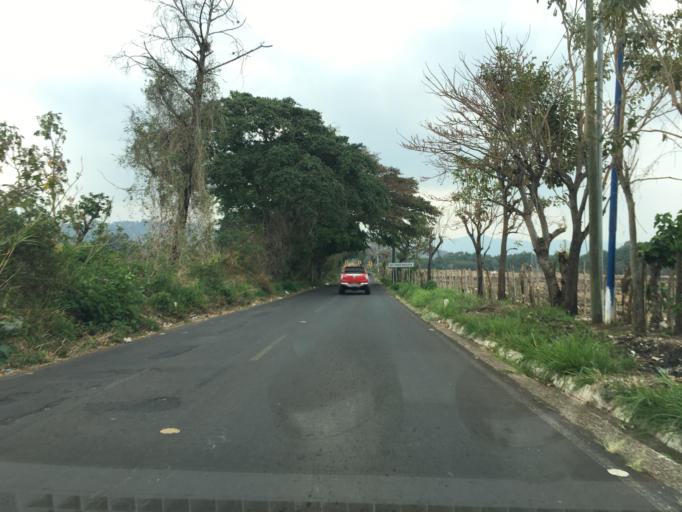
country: GT
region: Guatemala
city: Fraijanes
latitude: 14.3940
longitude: -90.4822
